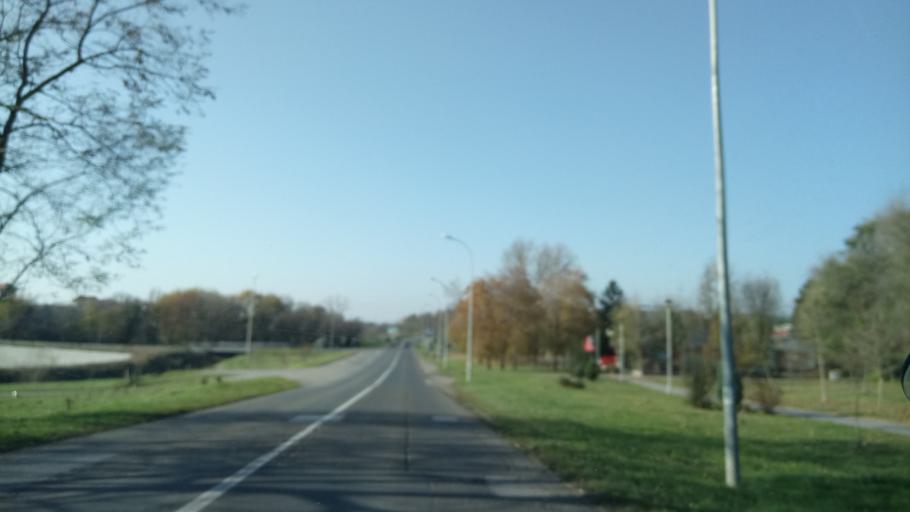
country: RS
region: Autonomna Pokrajina Vojvodina
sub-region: Sremski Okrug
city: Ingija
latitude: 45.0542
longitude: 20.0686
